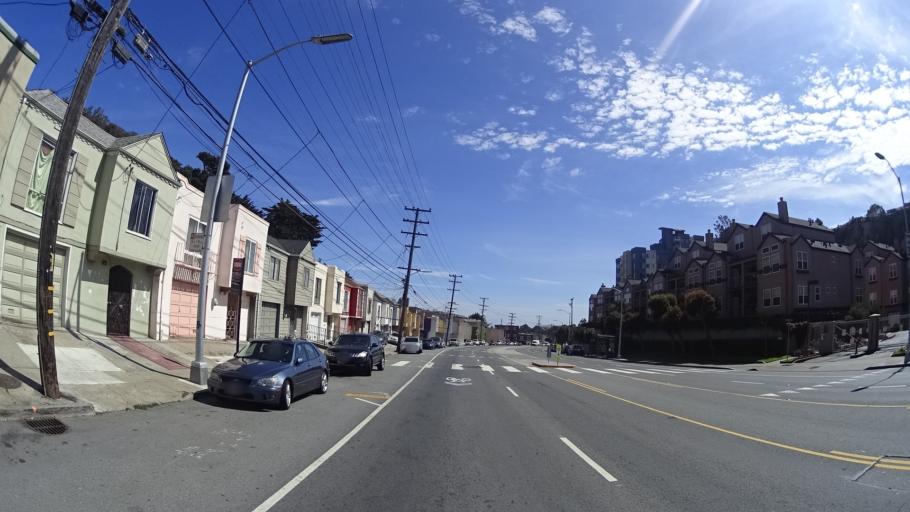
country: US
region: California
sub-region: San Mateo County
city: Daly City
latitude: 37.7110
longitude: -122.4262
